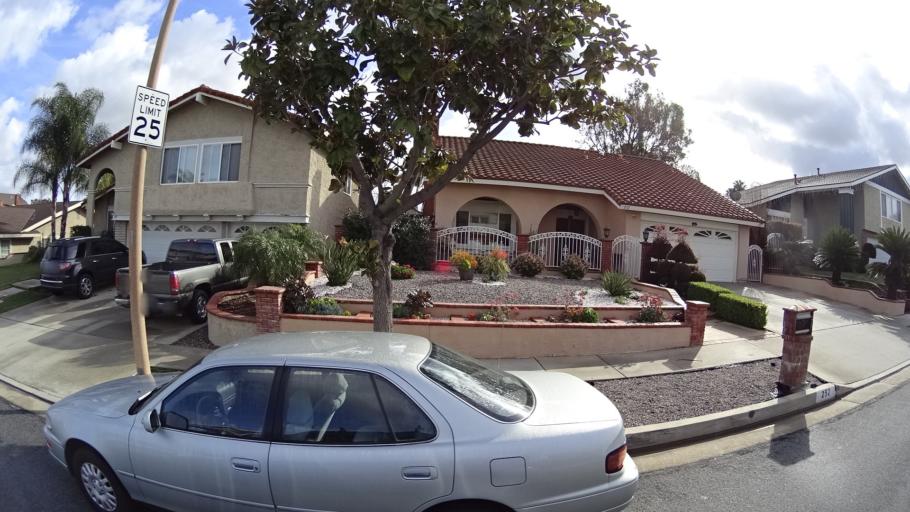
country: US
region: California
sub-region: Orange County
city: Villa Park
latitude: 33.8475
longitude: -117.7853
